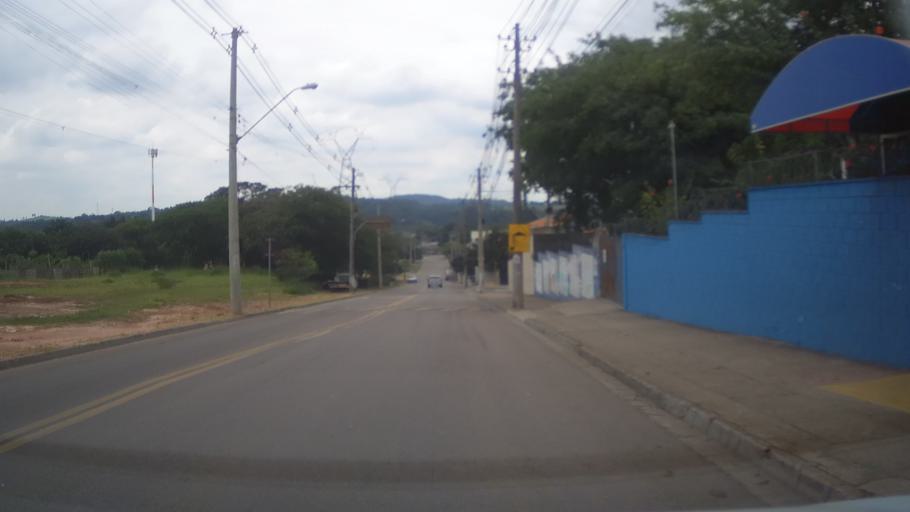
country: BR
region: Sao Paulo
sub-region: Itupeva
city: Itupeva
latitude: -23.1462
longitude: -46.9983
